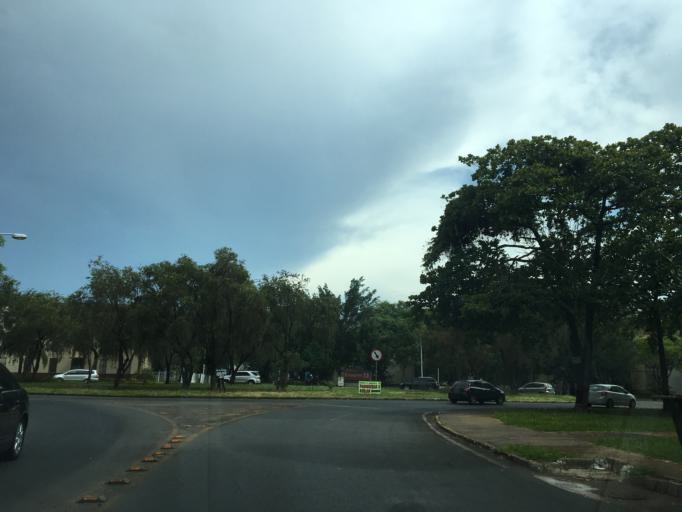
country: BR
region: Federal District
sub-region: Brasilia
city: Brasilia
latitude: -15.8274
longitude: -47.9101
